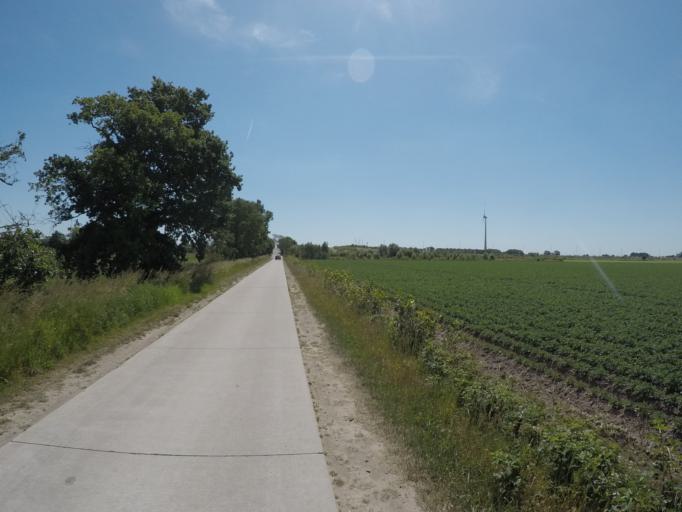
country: BE
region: Flanders
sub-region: Provincie Antwerpen
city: Hoogstraten
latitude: 51.4162
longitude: 4.6960
